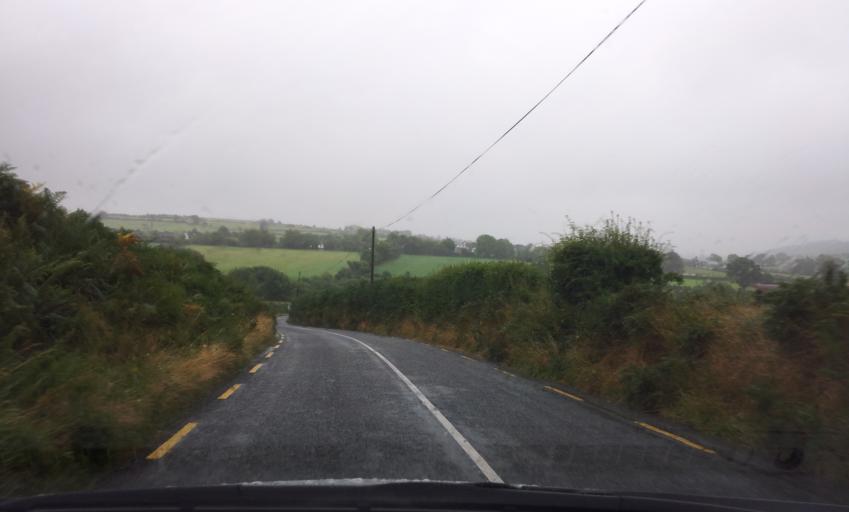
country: IE
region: Leinster
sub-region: Kilkenny
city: Thomastown
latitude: 52.4086
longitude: -7.0848
